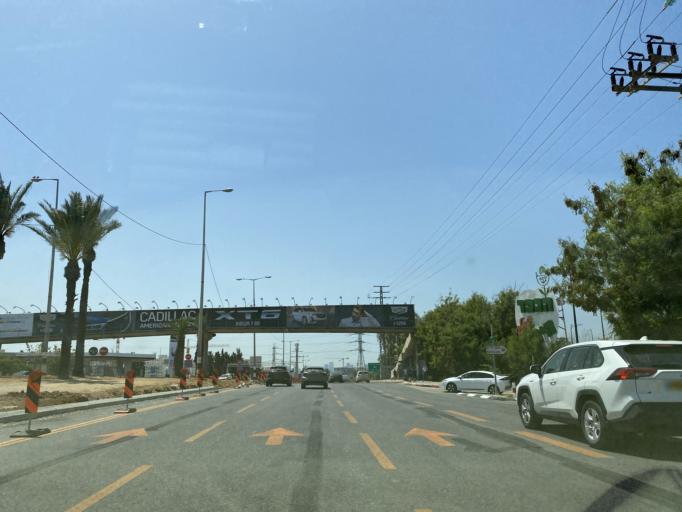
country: IL
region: Tel Aviv
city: Ramat HaSharon
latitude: 32.1333
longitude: 34.8323
